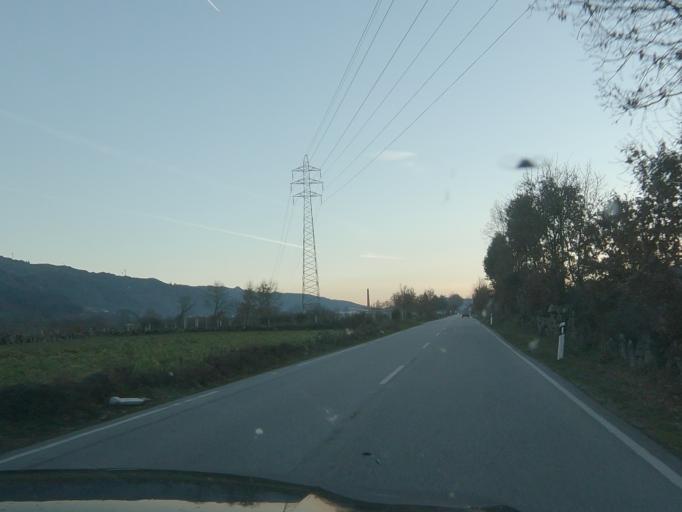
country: PT
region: Vila Real
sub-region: Vila Pouca de Aguiar
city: Vila Pouca de Aguiar
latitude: 41.4557
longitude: -7.6670
